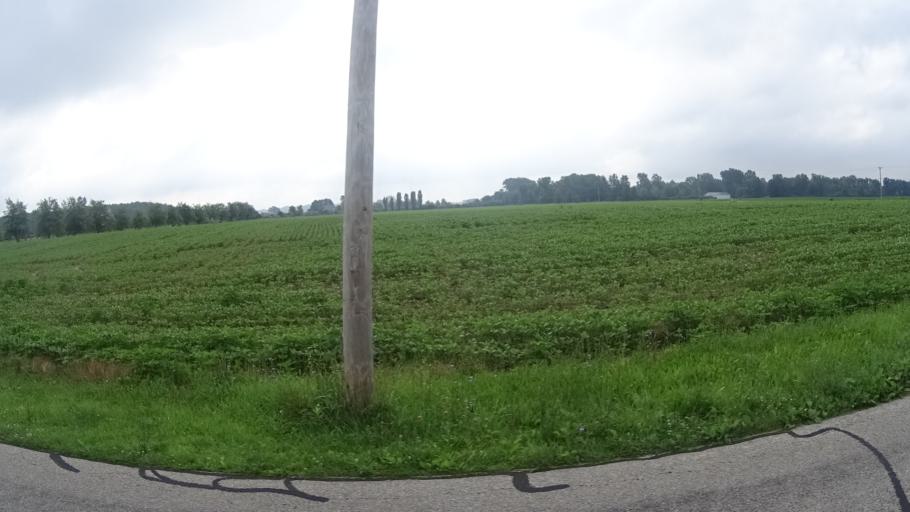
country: US
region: Ohio
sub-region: Erie County
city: Milan
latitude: 41.3048
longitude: -82.5095
